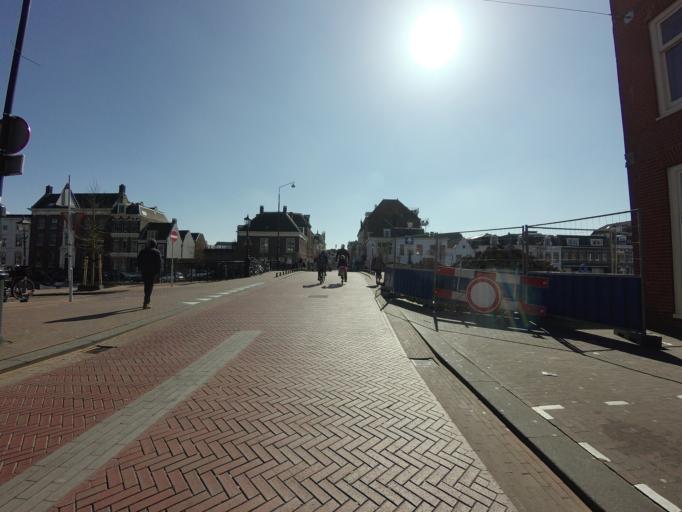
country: NL
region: North Holland
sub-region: Gemeente Haarlem
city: Haarlem
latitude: 52.3853
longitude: 4.6362
